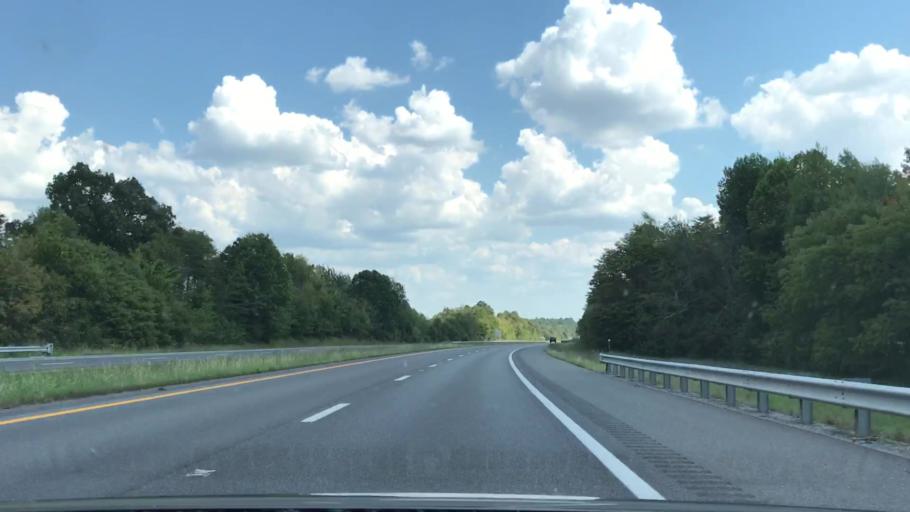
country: US
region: Kentucky
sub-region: Lyon County
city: Eddyville
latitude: 37.1098
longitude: -88.0221
